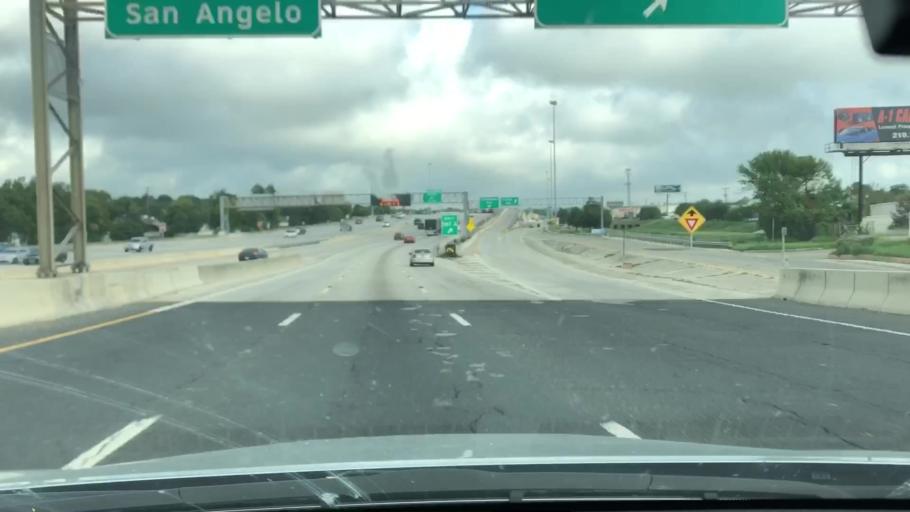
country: US
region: Texas
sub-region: Bexar County
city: Olmos Park
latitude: 29.4580
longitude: -98.5155
